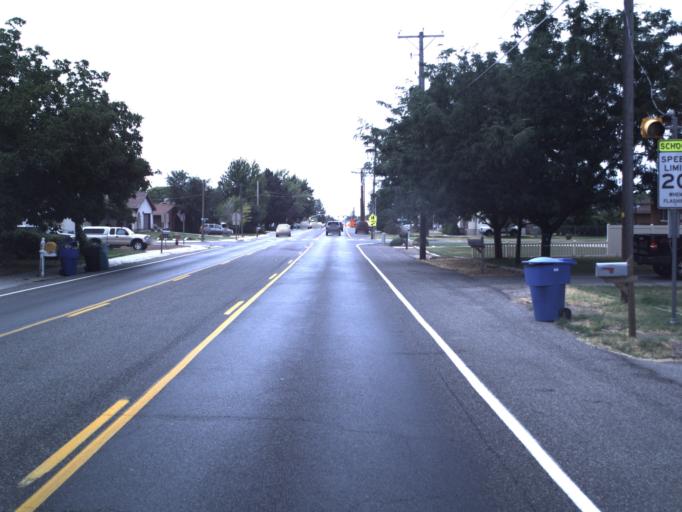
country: US
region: Utah
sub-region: Davis County
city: West Point
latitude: 41.1225
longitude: -112.0646
